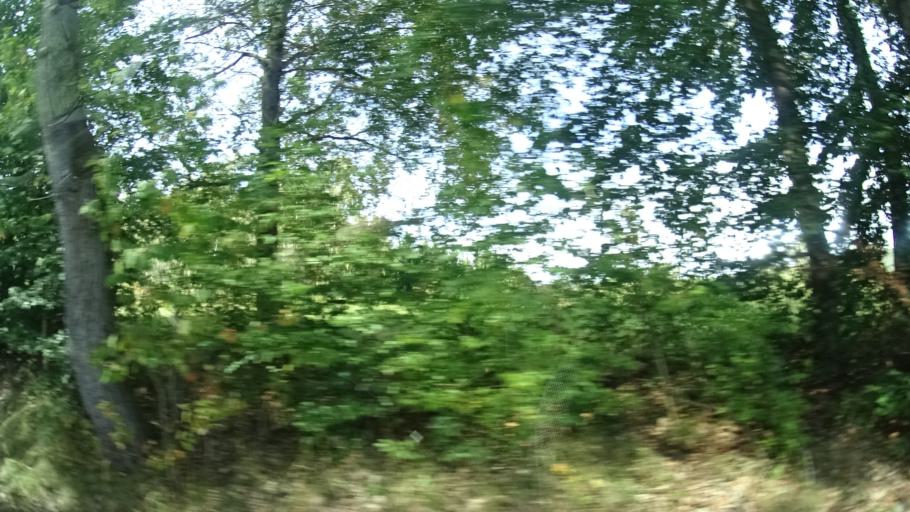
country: DE
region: Thuringia
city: Christes
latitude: 50.6584
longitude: 10.4669
